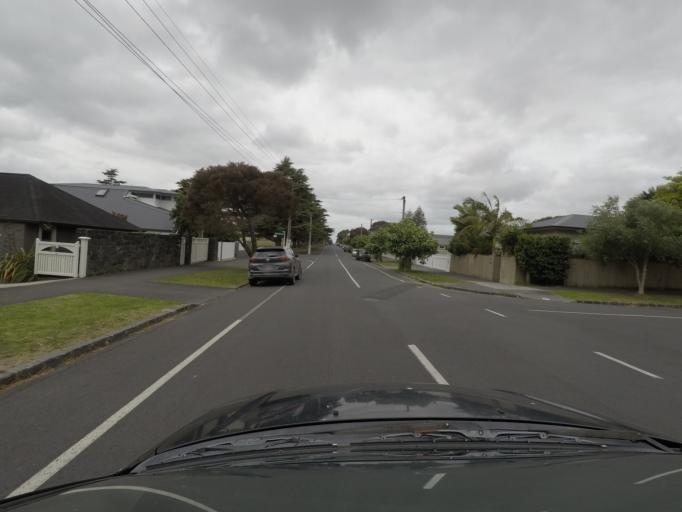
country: NZ
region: Auckland
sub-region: Auckland
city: Rosebank
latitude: -36.8666
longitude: 174.7023
